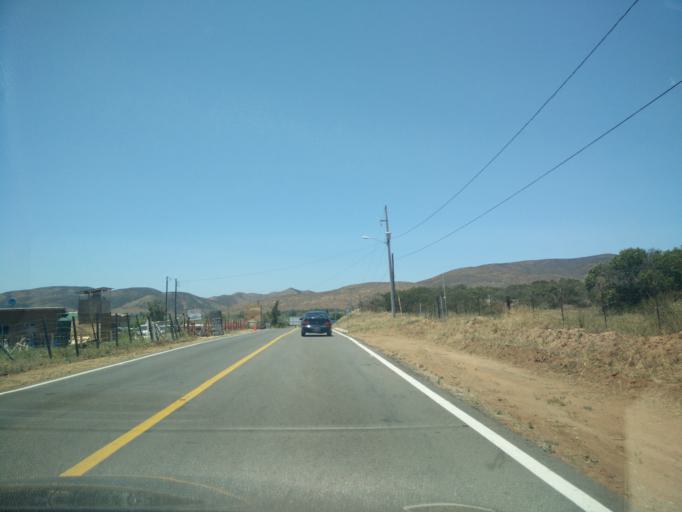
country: MX
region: Baja California
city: El Sauzal
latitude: 32.0063
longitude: -116.6775
